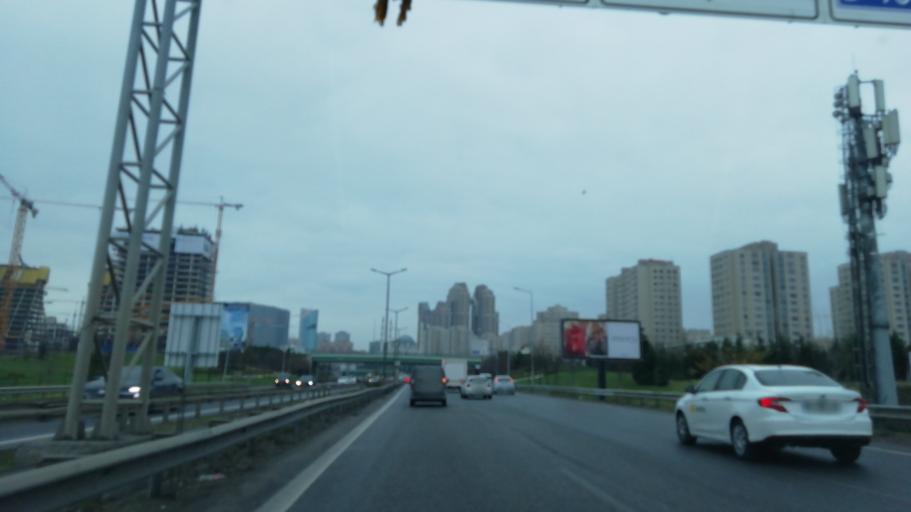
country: TR
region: Istanbul
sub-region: Atasehir
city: Atasehir
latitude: 41.0020
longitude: 29.1043
